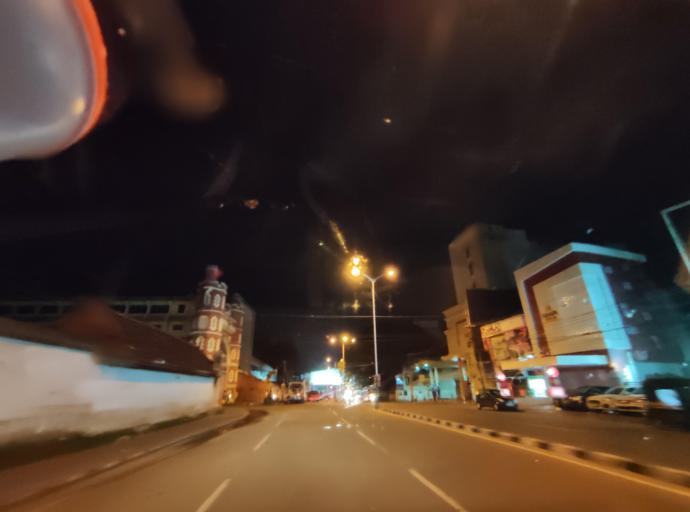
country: IN
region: Kerala
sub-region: Thiruvananthapuram
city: Thiruvananthapuram
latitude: 8.4802
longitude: 76.9474
